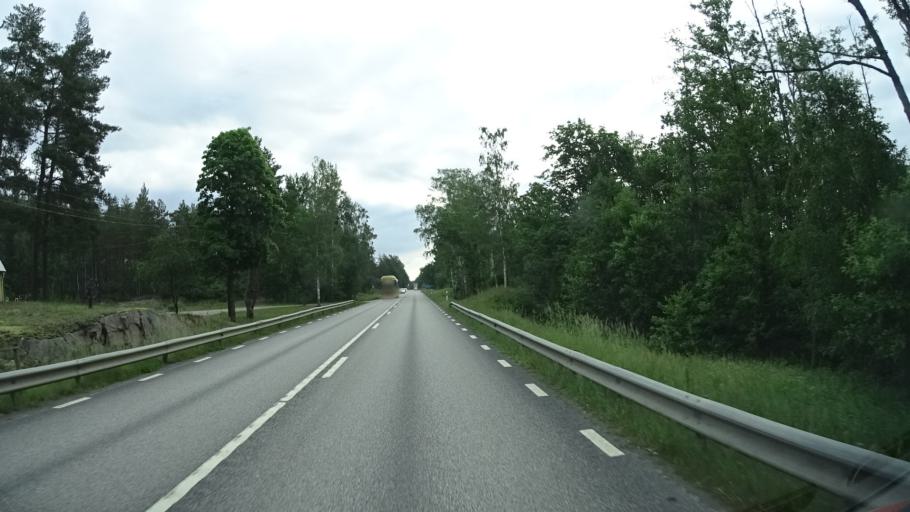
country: SE
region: Kalmar
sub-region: Oskarshamns Kommun
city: Oskarshamn
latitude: 57.2558
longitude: 16.3415
